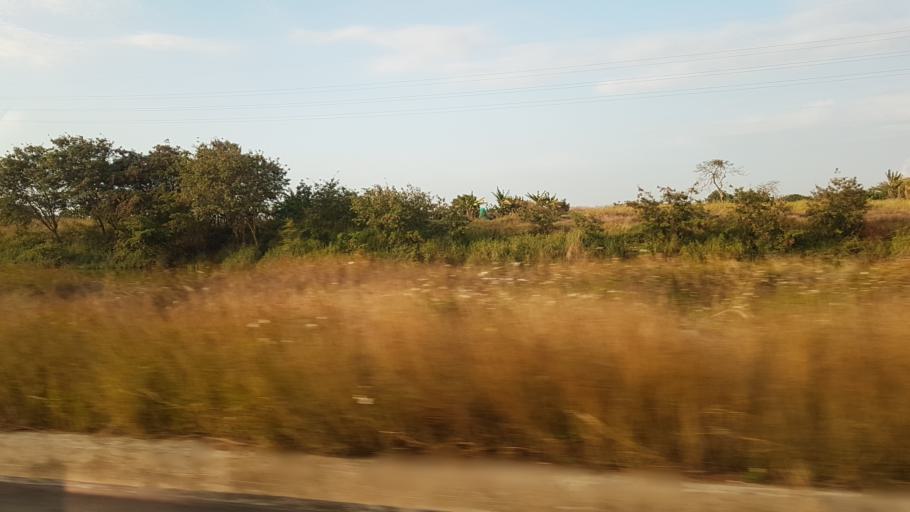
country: TW
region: Taiwan
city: Xinying
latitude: 23.3517
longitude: 120.3811
